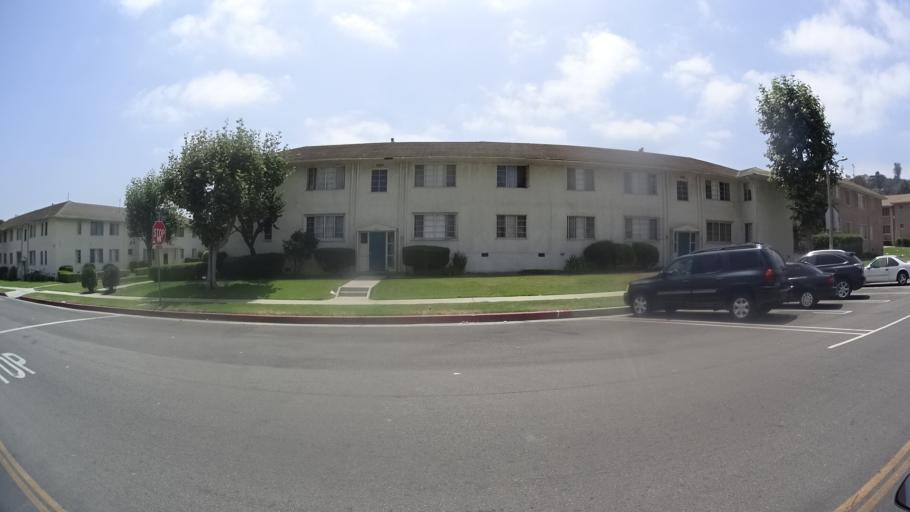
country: US
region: California
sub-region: Los Angeles County
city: View Park-Windsor Hills
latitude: 34.0126
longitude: -118.3478
